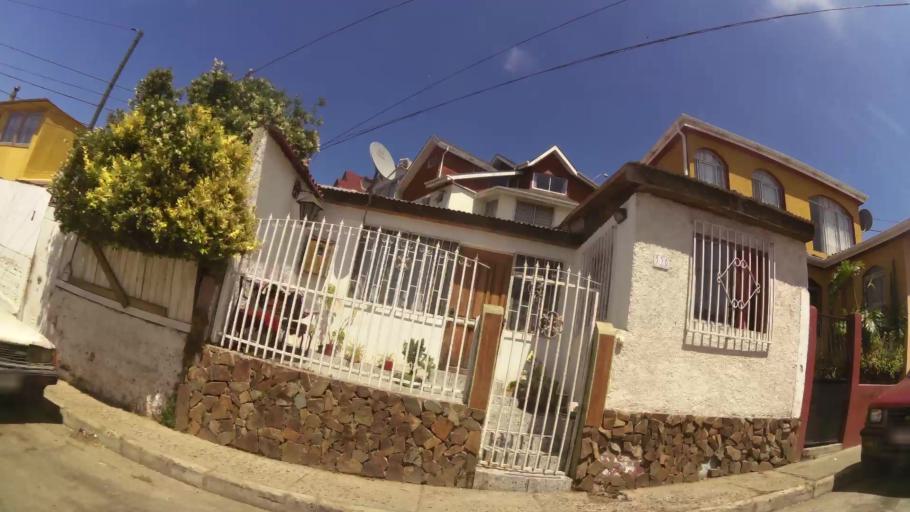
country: CL
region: Valparaiso
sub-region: Provincia de Valparaiso
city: Valparaiso
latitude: -33.0408
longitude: -71.6435
